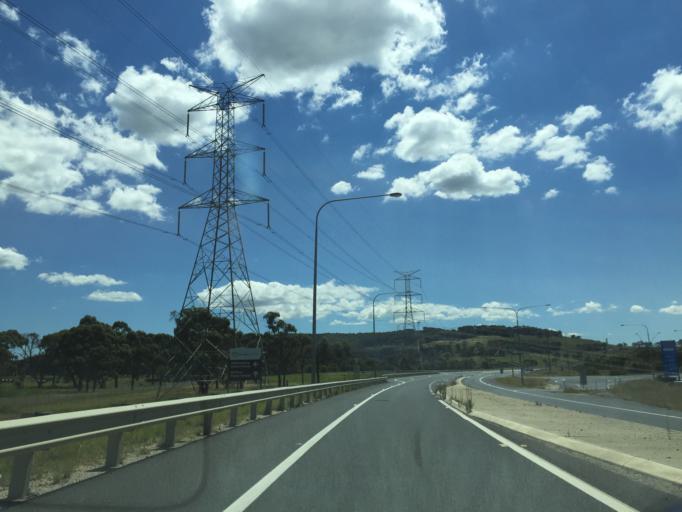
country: AU
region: New South Wales
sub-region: Lithgow
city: Lithgow
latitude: -33.3983
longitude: 150.0849
